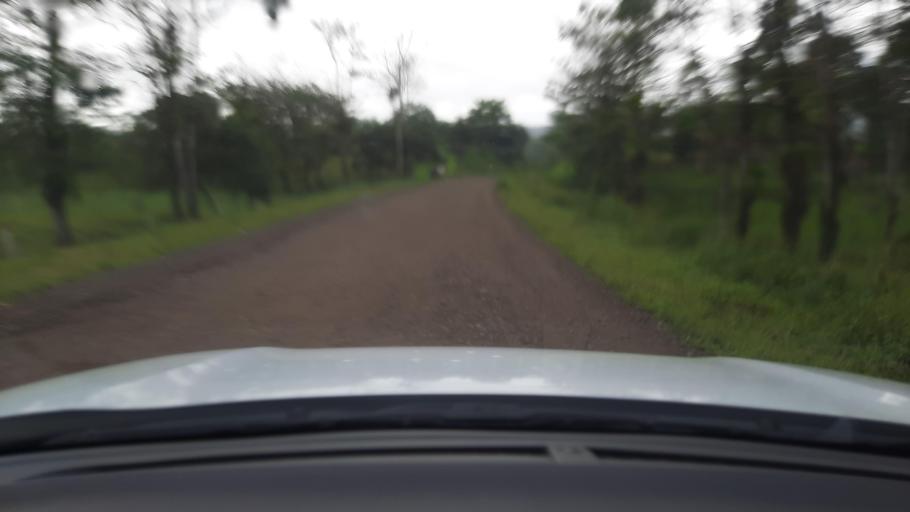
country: CR
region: Alajuela
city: San Jose
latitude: 11.0016
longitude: -85.2920
